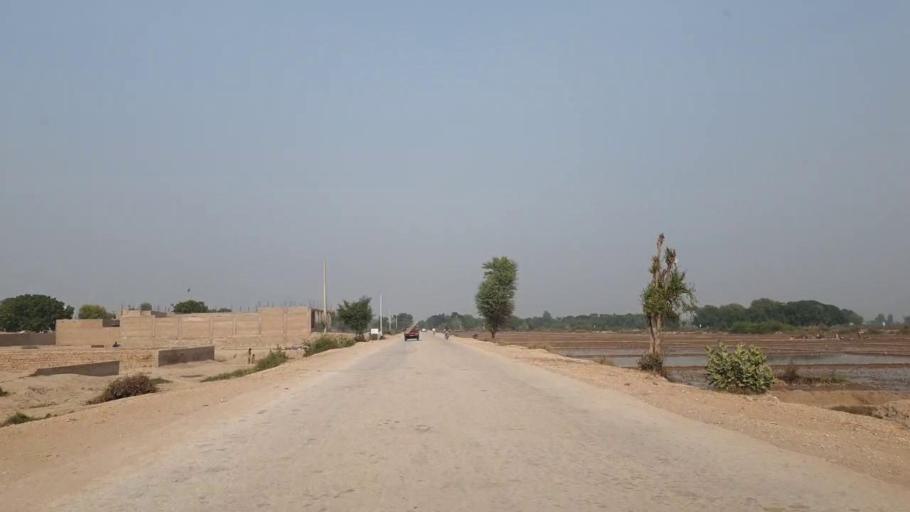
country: PK
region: Sindh
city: Bhan
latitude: 26.5693
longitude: 67.7257
